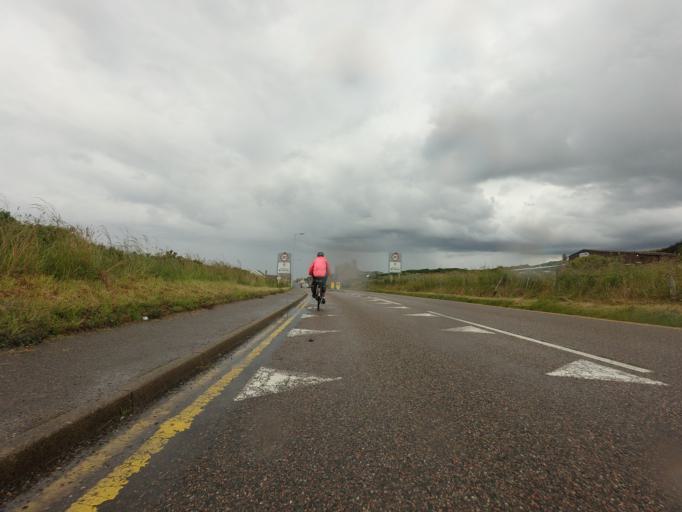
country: GB
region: Scotland
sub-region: Moray
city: Buckie
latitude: 57.6722
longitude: -2.9905
